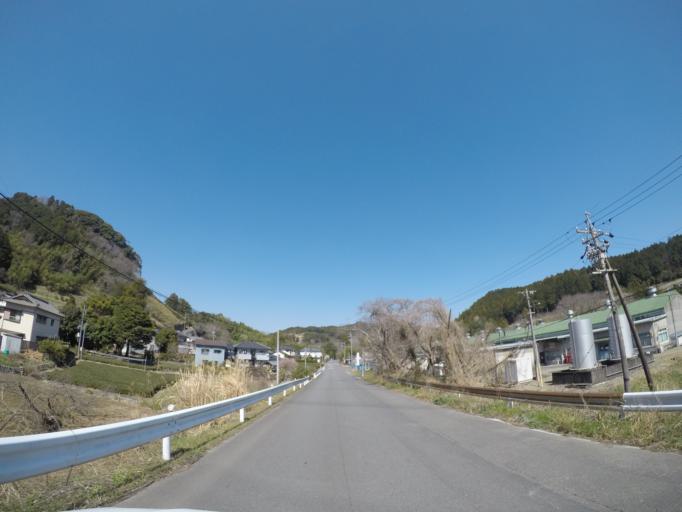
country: JP
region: Shizuoka
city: Kanaya
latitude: 34.7896
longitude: 138.1255
